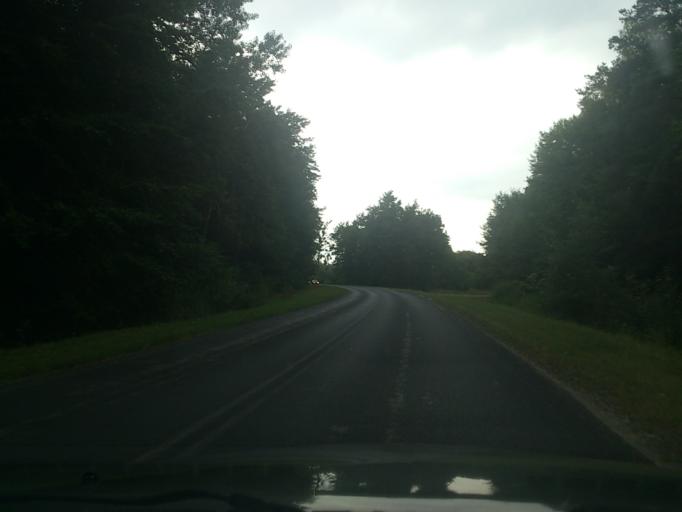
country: PL
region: Kujawsko-Pomorskie
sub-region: Powiat golubsko-dobrzynski
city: Golub-Dobrzyn
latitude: 53.0865
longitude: 19.0547
